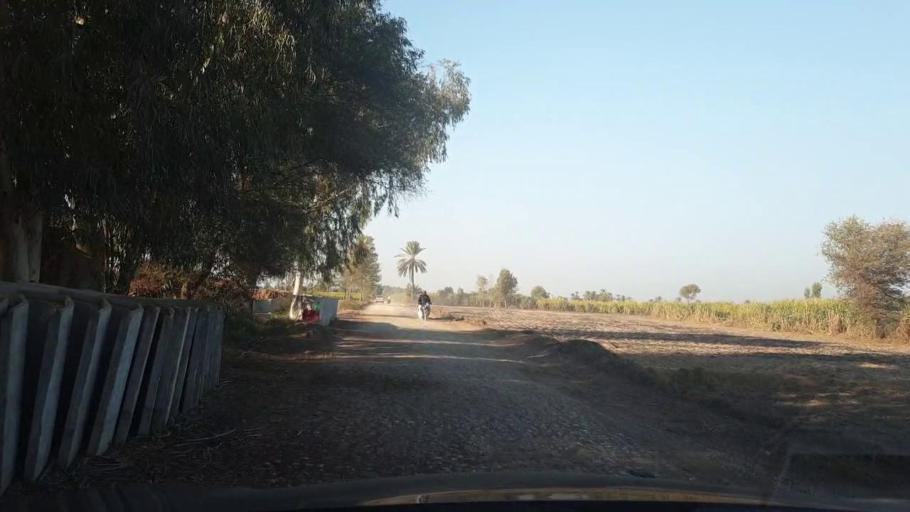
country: PK
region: Sindh
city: Ubauro
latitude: 28.1510
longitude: 69.6089
